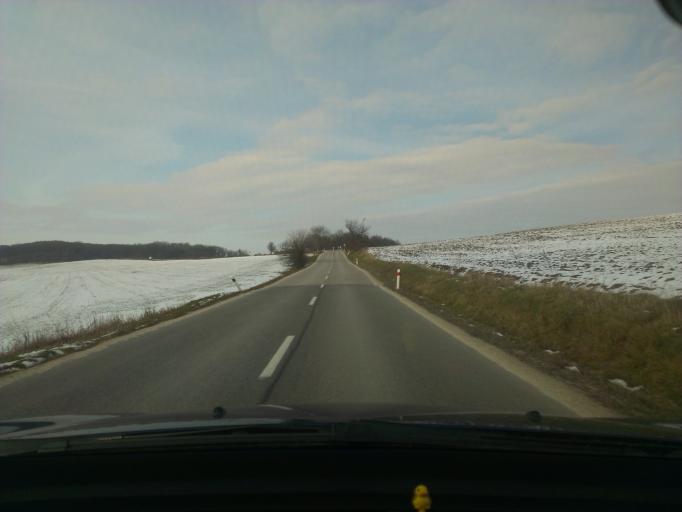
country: SK
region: Nitriansky
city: Stara Tura
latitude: 48.7143
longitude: 17.6856
